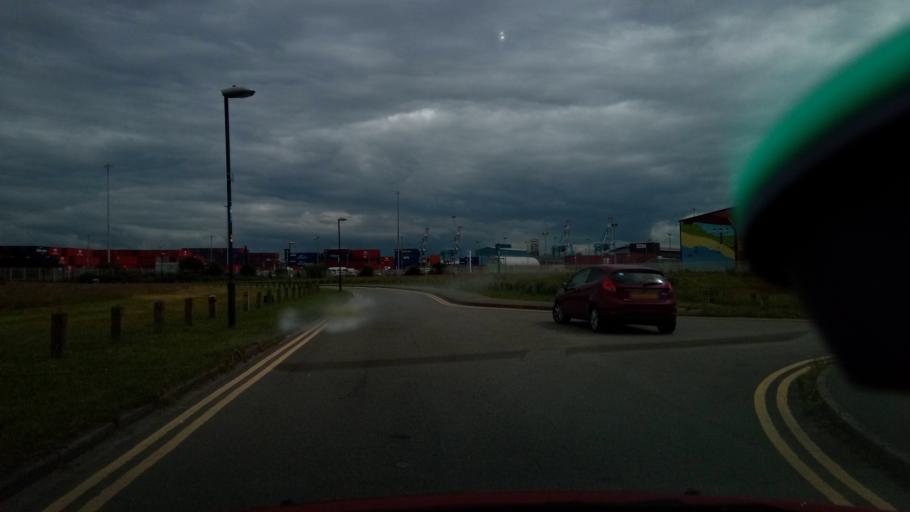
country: GB
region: England
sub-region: Sefton
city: Waterloo
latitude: 53.4692
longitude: -3.0267
